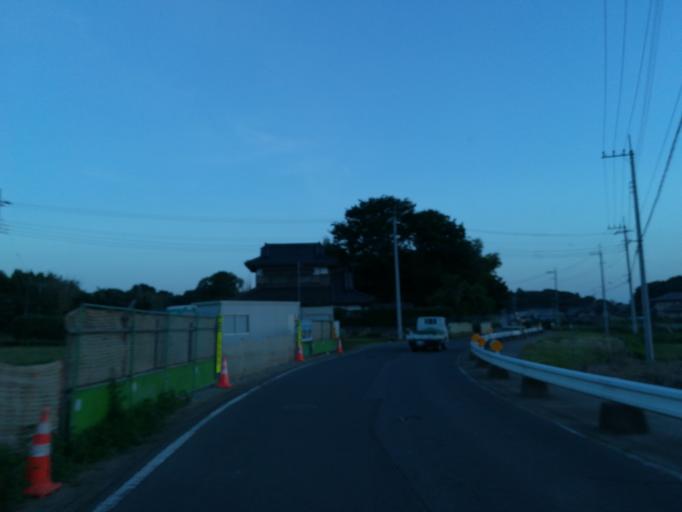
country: JP
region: Ibaraki
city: Makabe
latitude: 36.2899
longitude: 140.0600
